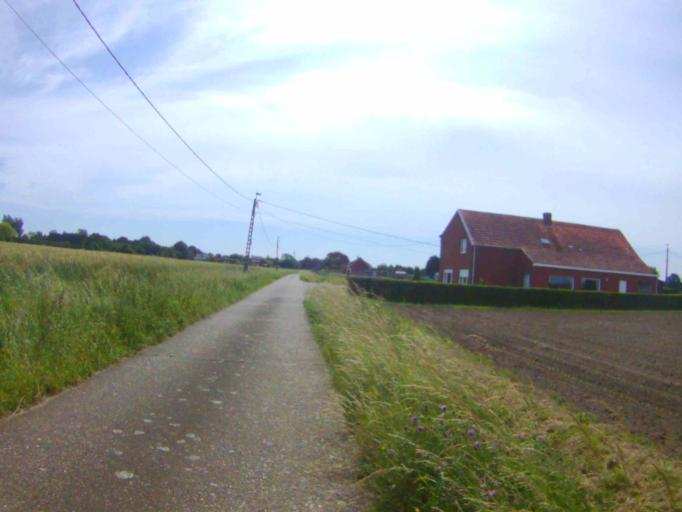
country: BE
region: Flanders
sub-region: Provincie Antwerpen
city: Putte
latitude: 51.0864
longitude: 4.6364
